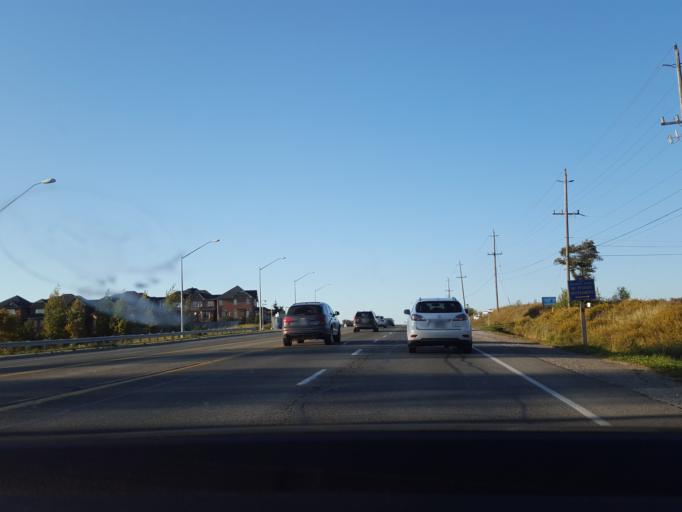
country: CA
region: Ontario
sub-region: York
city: Richmond Hill
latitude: 43.9227
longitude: -79.4494
